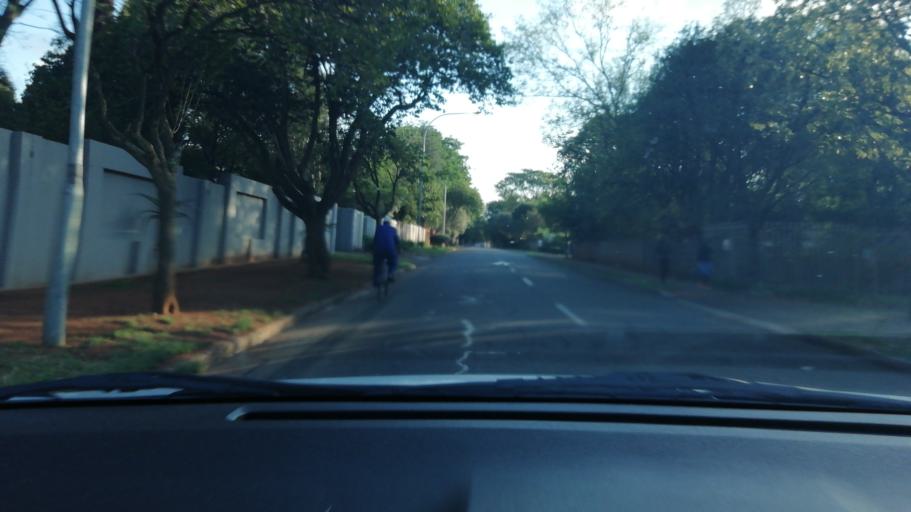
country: ZA
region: Gauteng
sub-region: Ekurhuleni Metropolitan Municipality
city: Benoni
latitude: -26.1980
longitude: 28.2981
